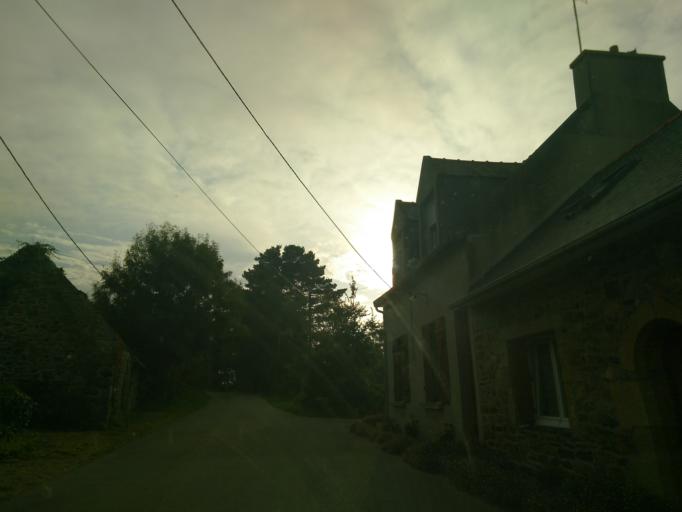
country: FR
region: Brittany
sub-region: Departement du Finistere
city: Crozon
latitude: 48.2392
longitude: -4.4555
